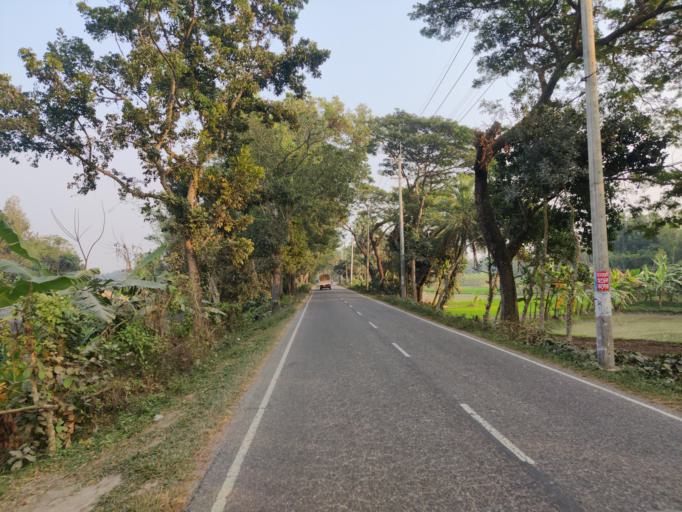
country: BD
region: Dhaka
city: Narsingdi
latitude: 24.0948
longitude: 90.7204
